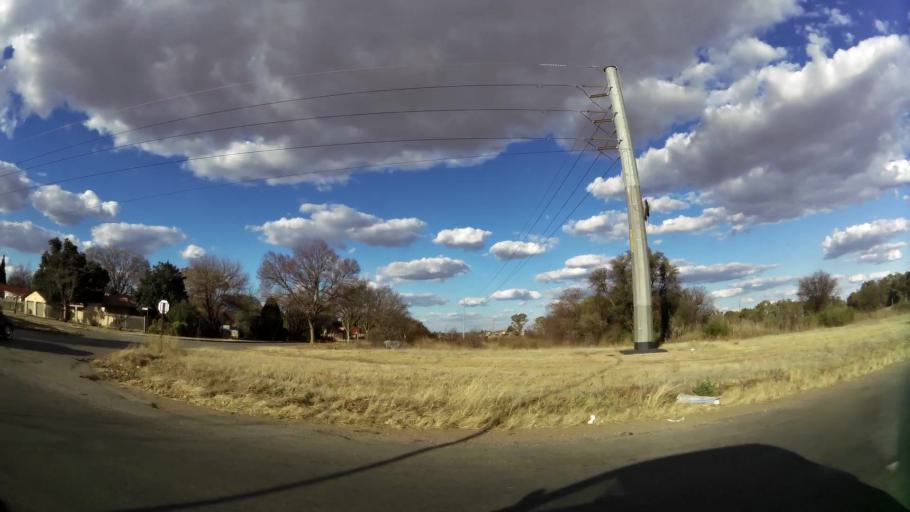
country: ZA
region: North-West
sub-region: Dr Kenneth Kaunda District Municipality
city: Potchefstroom
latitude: -26.7034
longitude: 27.0781
